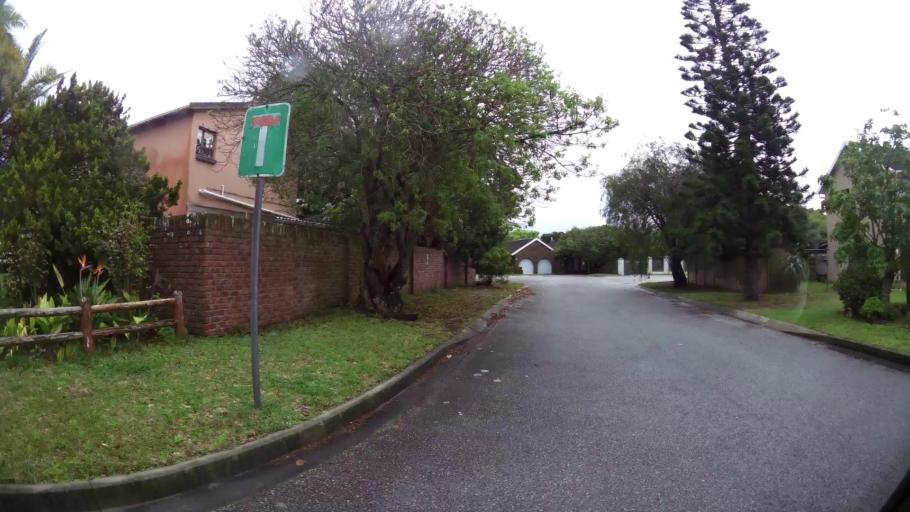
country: ZA
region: Eastern Cape
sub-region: Nelson Mandela Bay Metropolitan Municipality
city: Port Elizabeth
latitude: -33.9951
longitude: 25.5533
